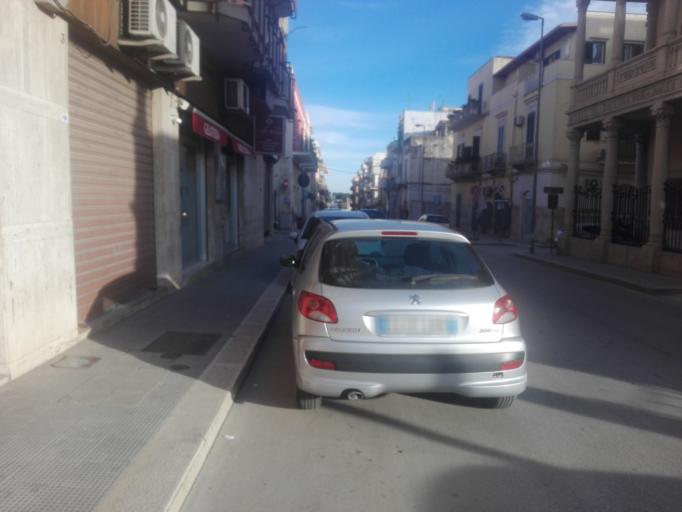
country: IT
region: Apulia
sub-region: Provincia di Bari
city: Corato
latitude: 41.1516
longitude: 16.4169
